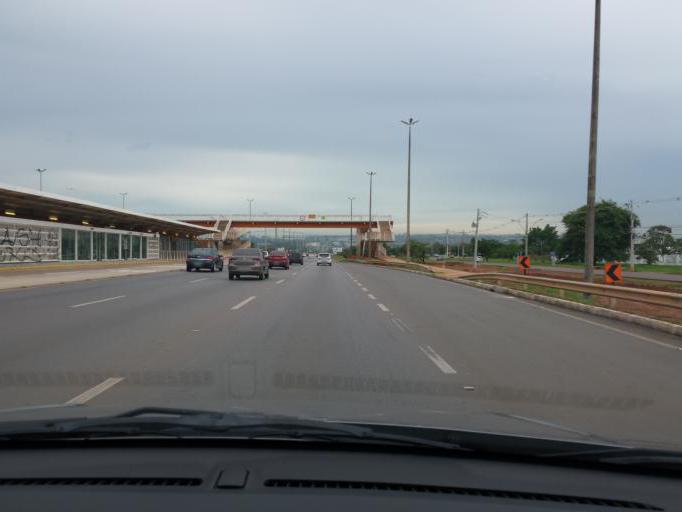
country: BR
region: Federal District
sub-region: Brasilia
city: Brasilia
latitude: -15.8915
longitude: -47.9613
